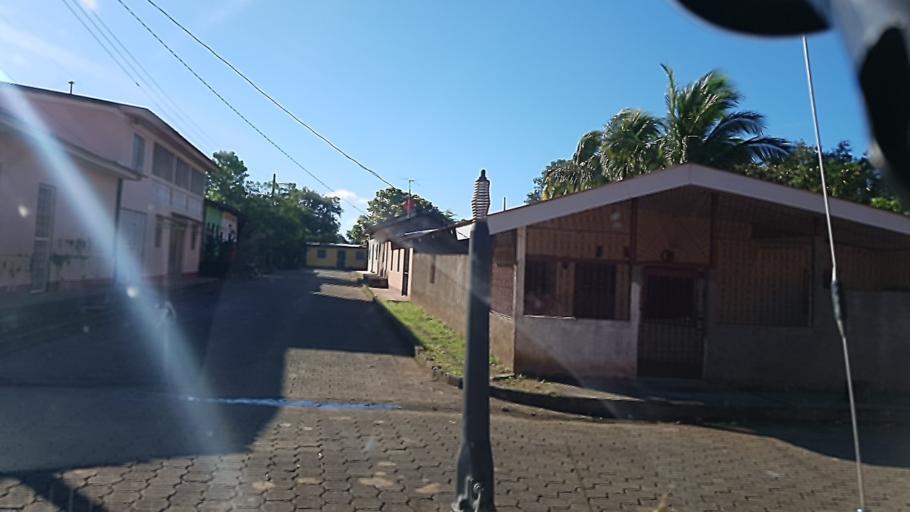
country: NI
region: Carazo
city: Santa Teresa
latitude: 11.7343
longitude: -86.1927
